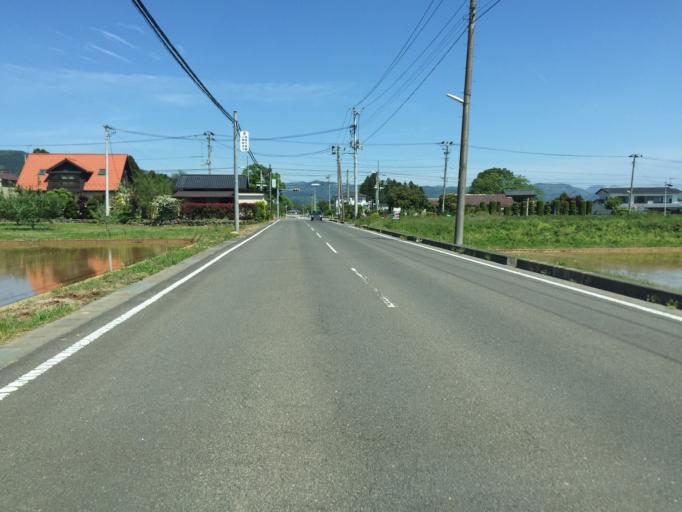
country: JP
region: Fukushima
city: Fukushima-shi
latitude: 37.7187
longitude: 140.3792
